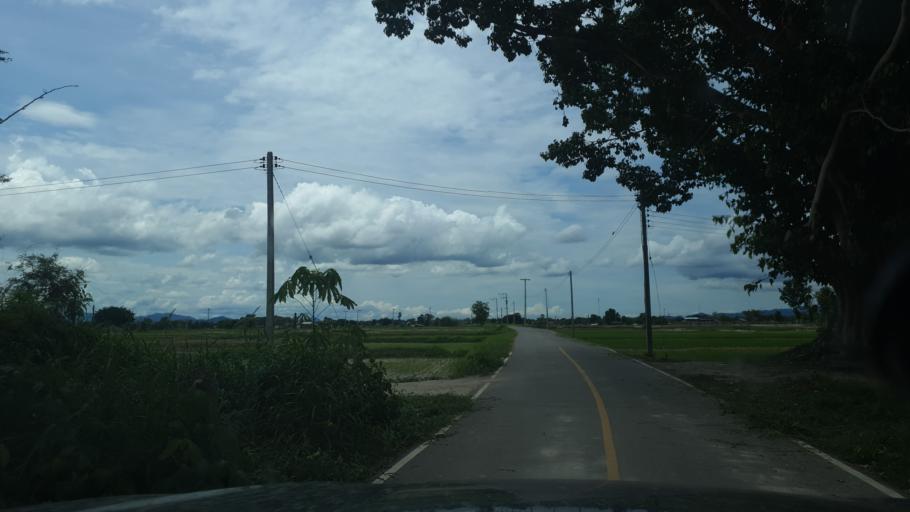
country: TH
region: Lampang
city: Sop Prap
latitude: 17.8693
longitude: 99.3873
